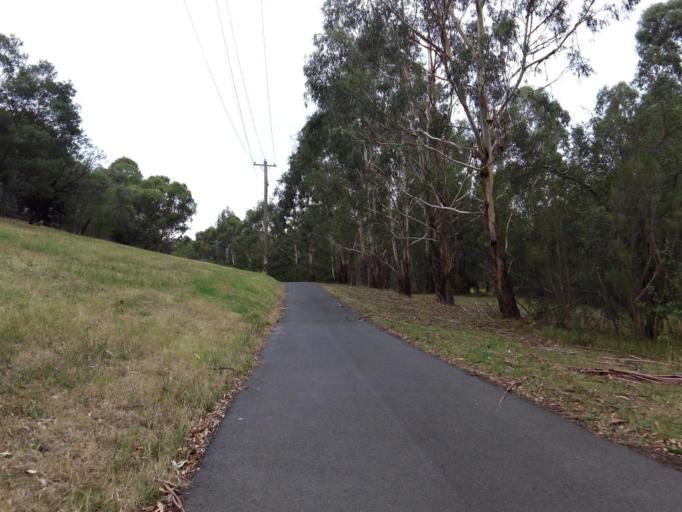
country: AU
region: Victoria
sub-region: Manningham
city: Templestowe Lower
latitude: -37.7624
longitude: 145.1272
